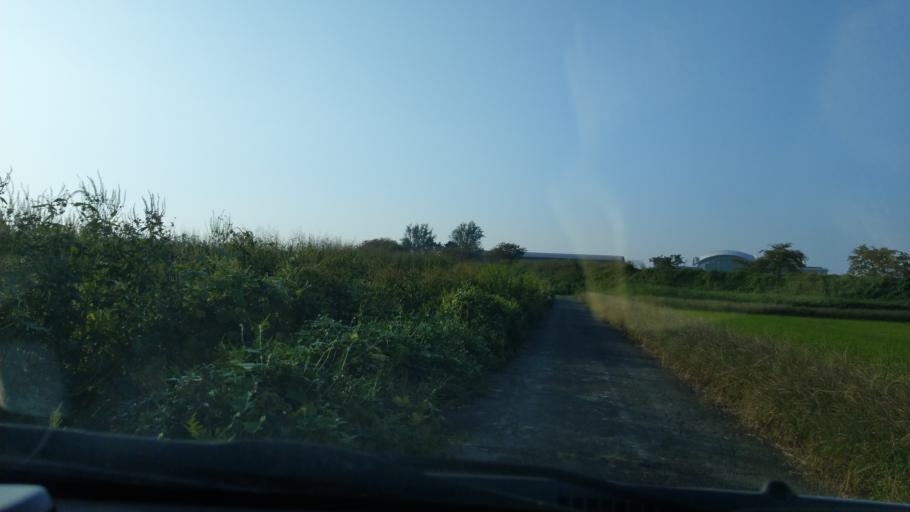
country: JP
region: Saitama
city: Shiki
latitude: 35.8523
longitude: 139.6128
